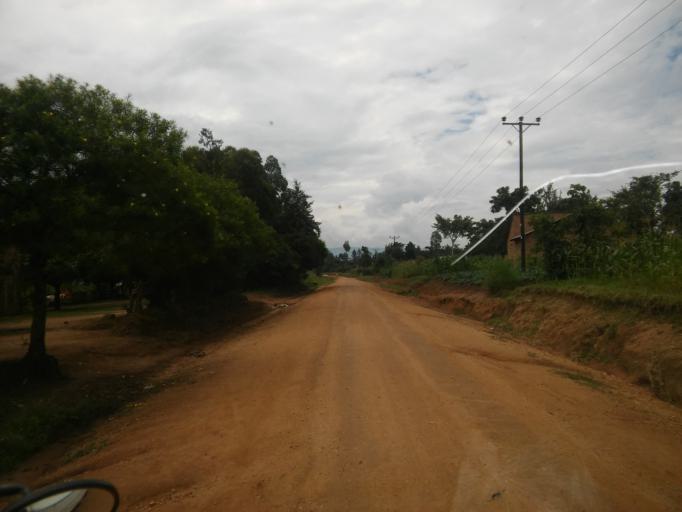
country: KE
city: Malikisi
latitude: 0.8180
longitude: 34.3500
